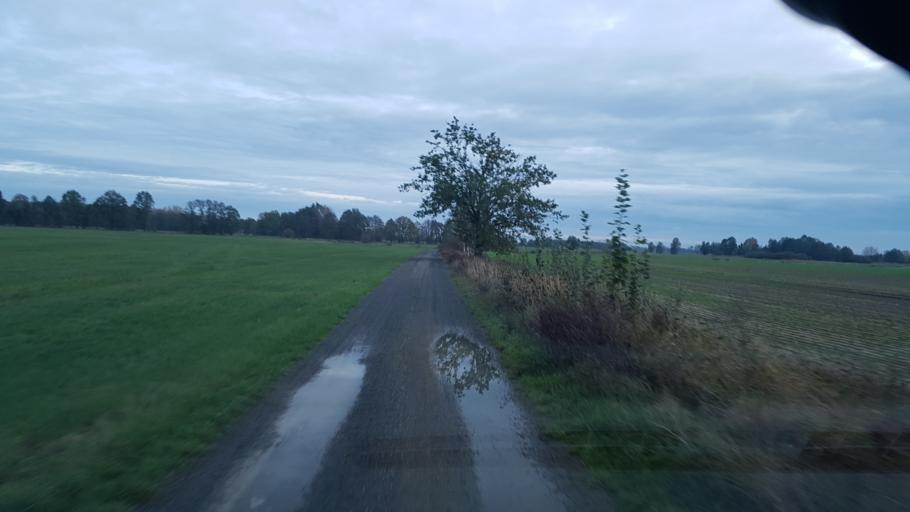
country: DE
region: Brandenburg
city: Falkenberg
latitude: 51.5341
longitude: 13.2766
